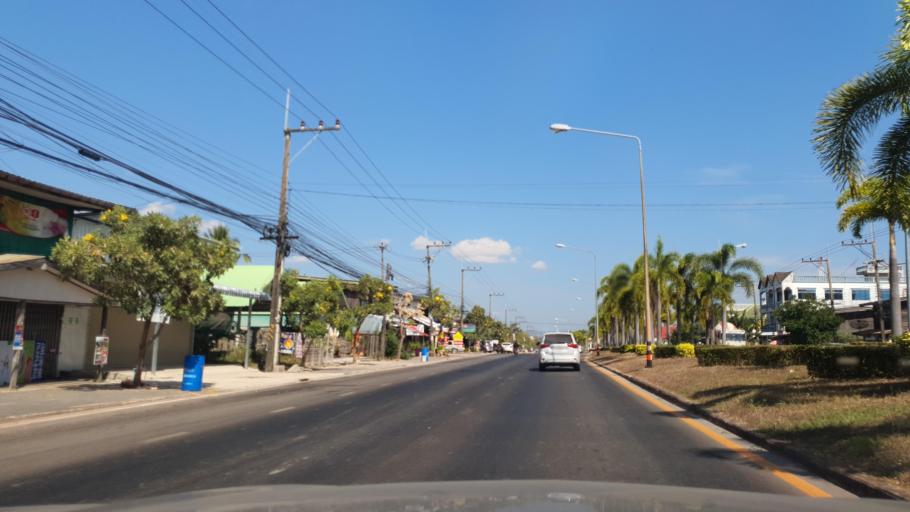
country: TH
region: Kalasin
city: Somdet
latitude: 16.7025
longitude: 103.7473
